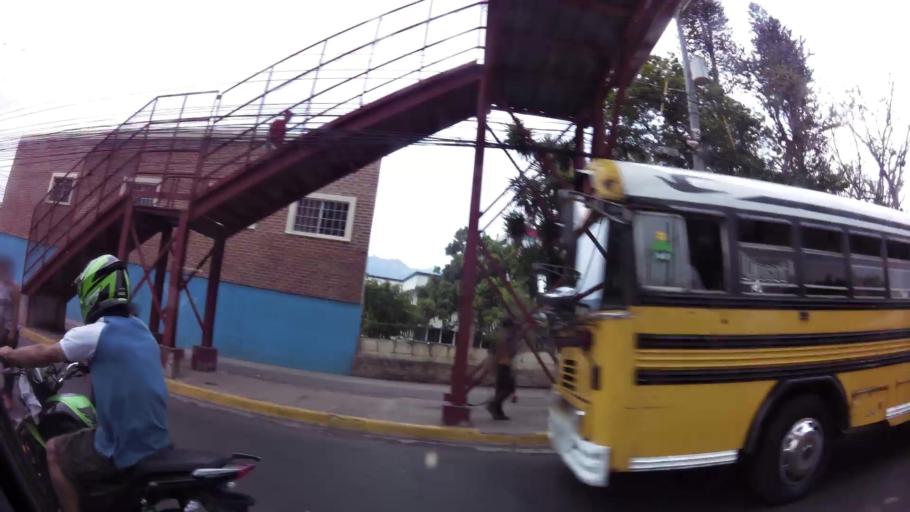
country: HN
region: Francisco Morazan
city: Tegucigalpa
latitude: 14.1030
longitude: -87.1867
